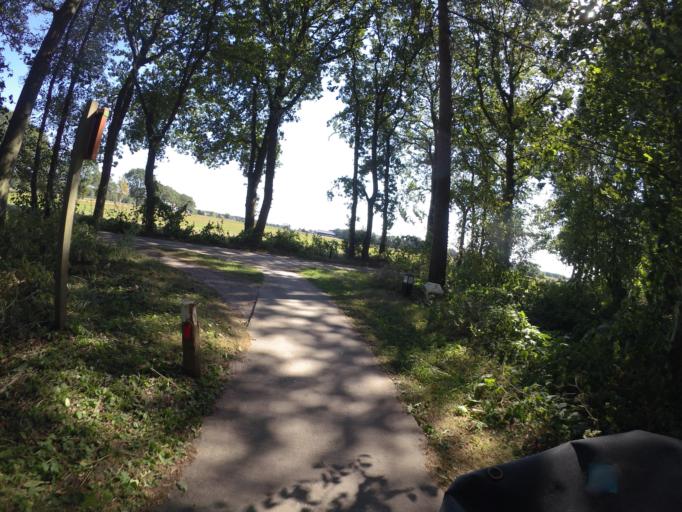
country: NL
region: Friesland
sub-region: Gemeente Gaasterlan-Sleat
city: Oudemirdum
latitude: 52.8639
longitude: 5.5586
